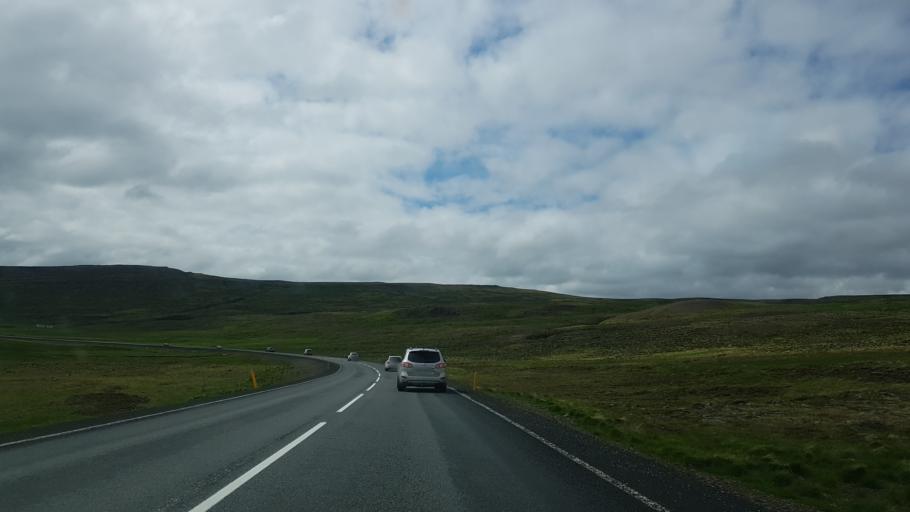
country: IS
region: West
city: Borgarnes
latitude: 64.9079
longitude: -21.1712
